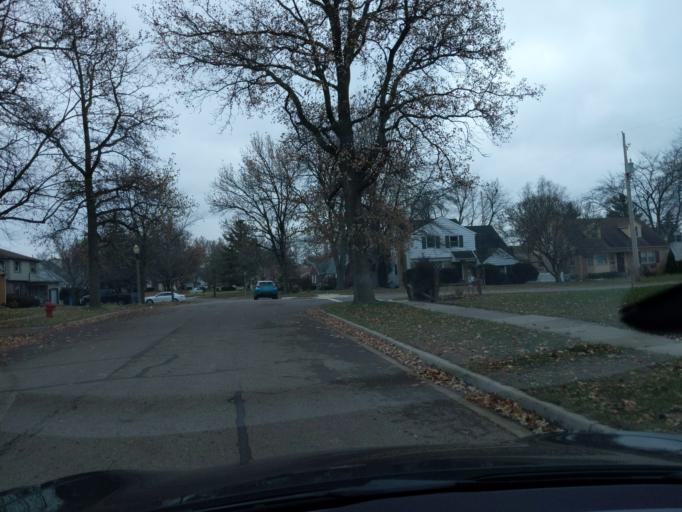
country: US
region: Michigan
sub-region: Ingham County
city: Lansing
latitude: 42.7080
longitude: -84.5812
